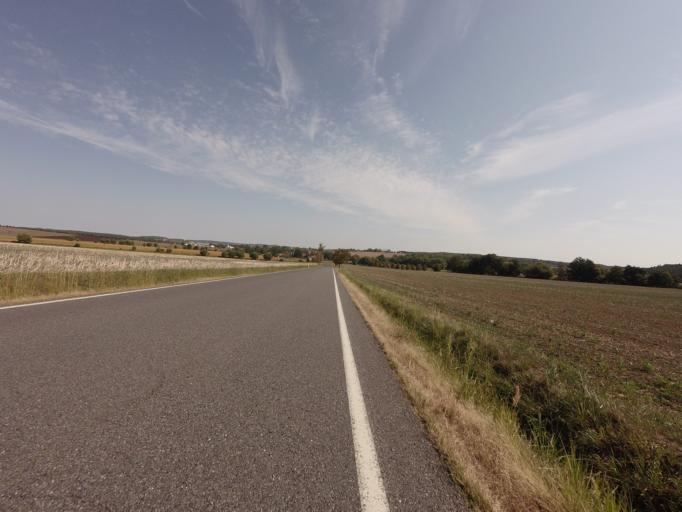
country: CZ
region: Jihocesky
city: Bernartice
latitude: 49.3525
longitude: 14.3742
